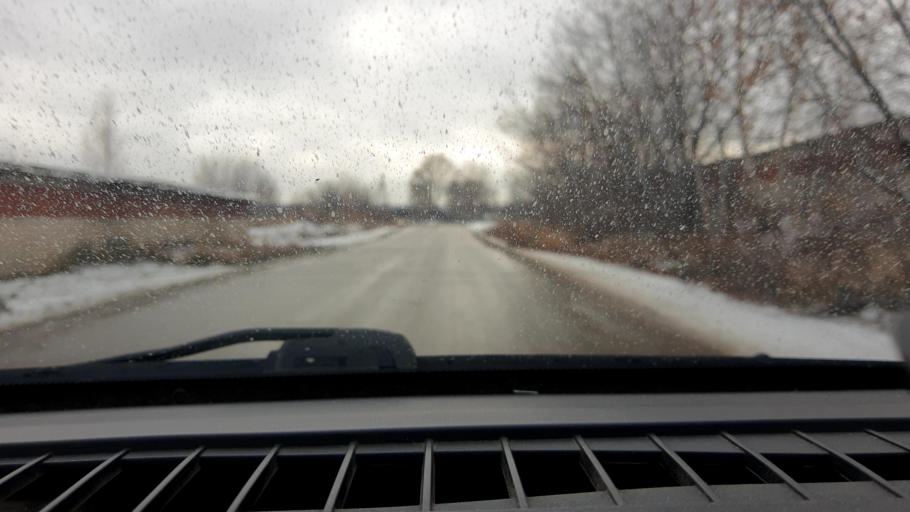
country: RU
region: Nizjnij Novgorod
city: Taremskoye
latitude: 55.9356
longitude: 43.0589
